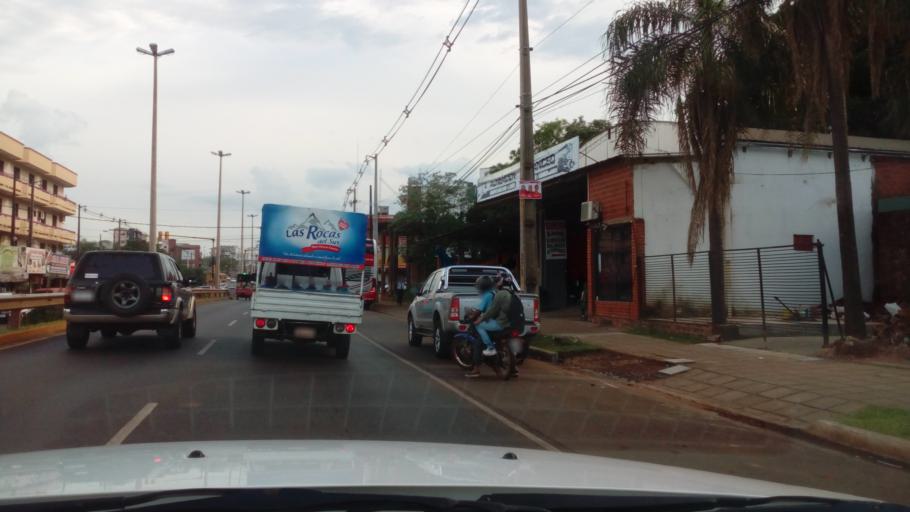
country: PY
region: Itapua
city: Encarnacion
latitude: -27.3464
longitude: -55.8584
